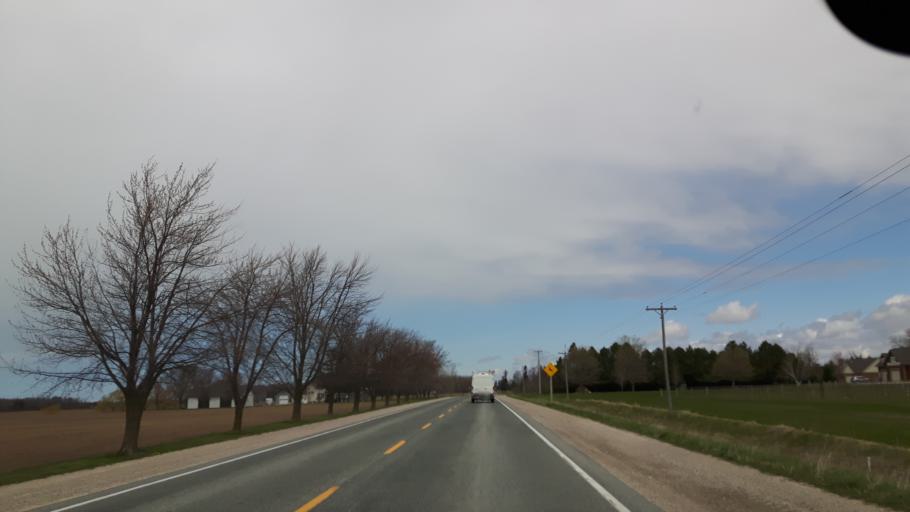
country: CA
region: Ontario
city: Bluewater
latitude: 43.4920
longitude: -81.6965
